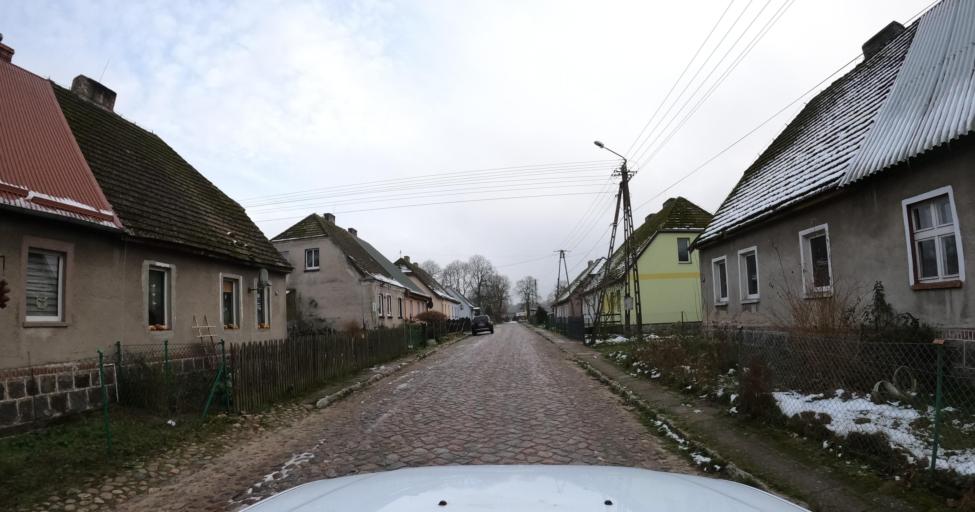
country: PL
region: West Pomeranian Voivodeship
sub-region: Powiat swidwinski
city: Swidwin
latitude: 53.8719
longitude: 15.8303
